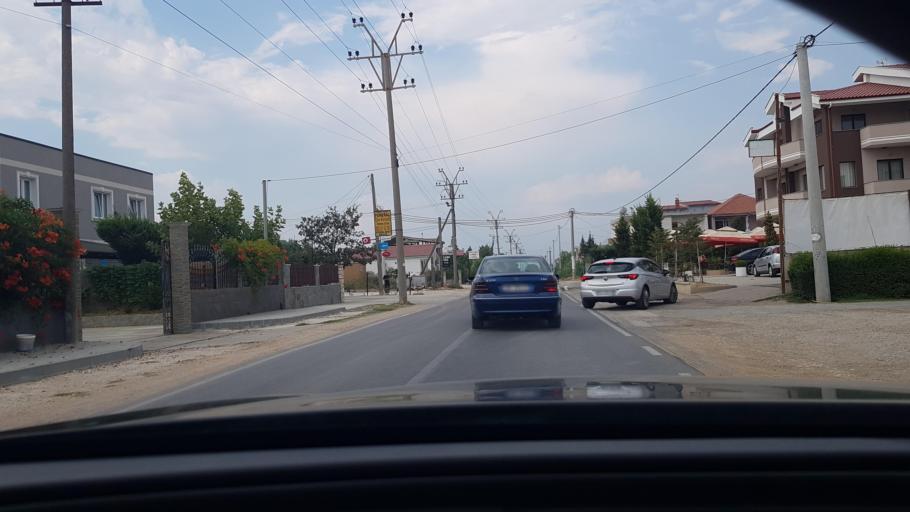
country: AL
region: Durres
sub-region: Rrethi i Durresit
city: Sukth
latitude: 41.4013
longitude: 19.5466
